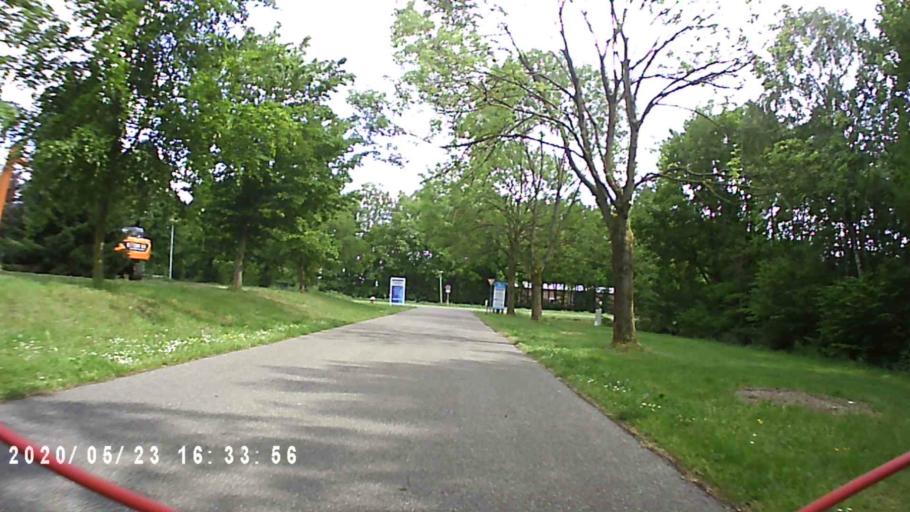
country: NL
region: Groningen
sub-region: Gemeente Slochteren
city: Slochteren
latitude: 53.2665
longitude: 6.8370
